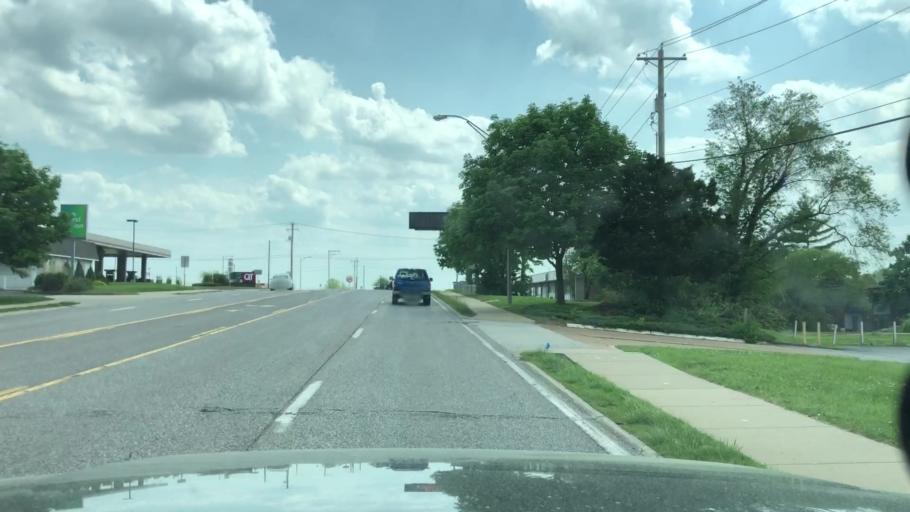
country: US
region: Missouri
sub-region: Saint Charles County
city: Saint Charles
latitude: 38.7796
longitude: -90.5087
